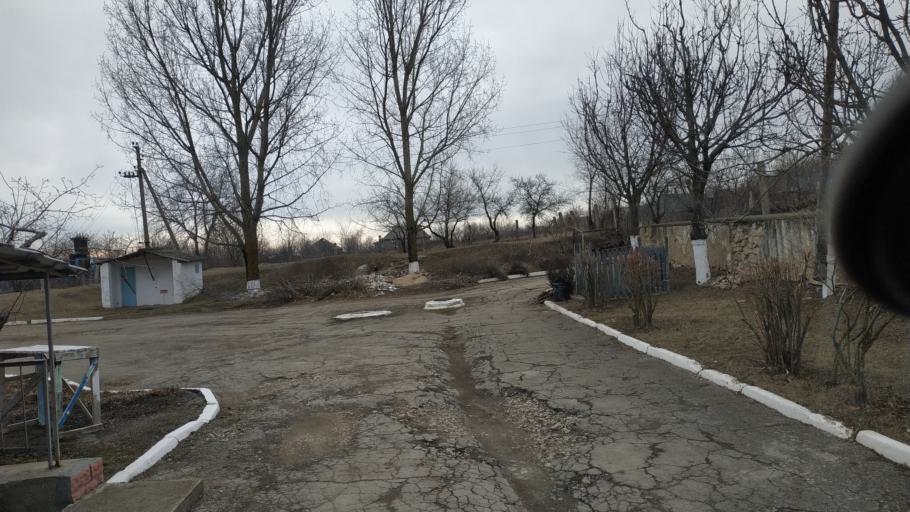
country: MD
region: Telenesti
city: Cocieri
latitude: 47.3119
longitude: 29.0706
